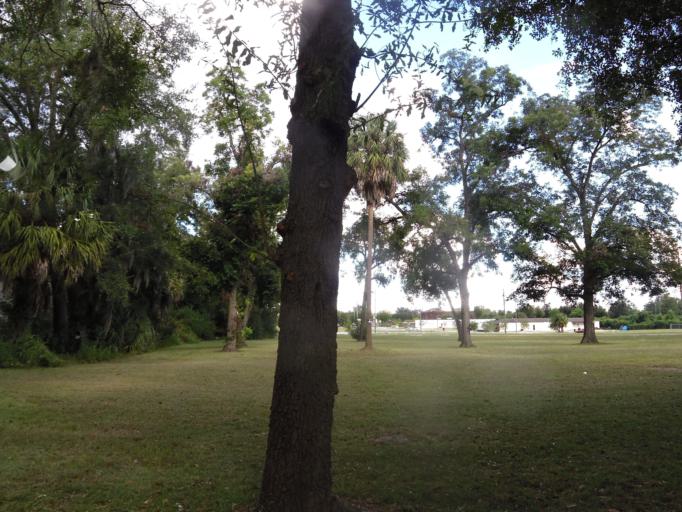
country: US
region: Georgia
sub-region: Lowndes County
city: Valdosta
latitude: 30.8289
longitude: -83.2856
